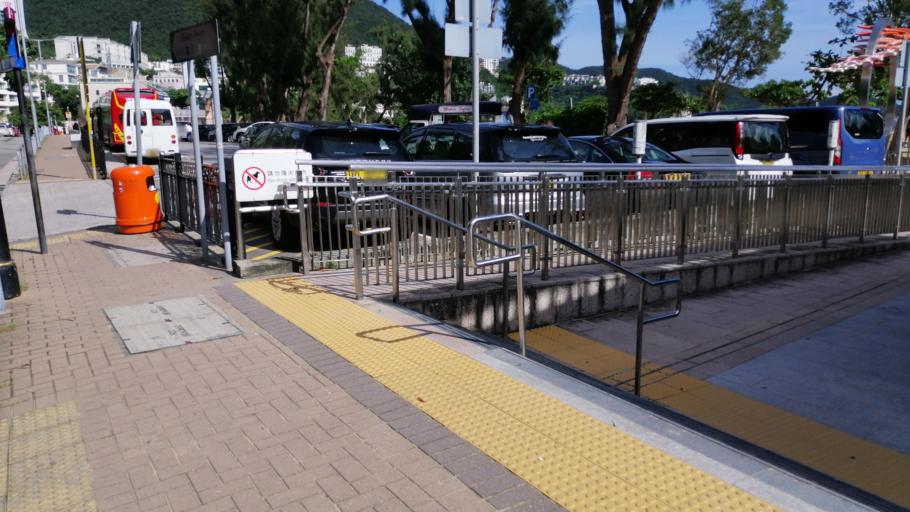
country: HK
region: Wanchai
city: Wan Chai
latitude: 22.2380
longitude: 114.1958
